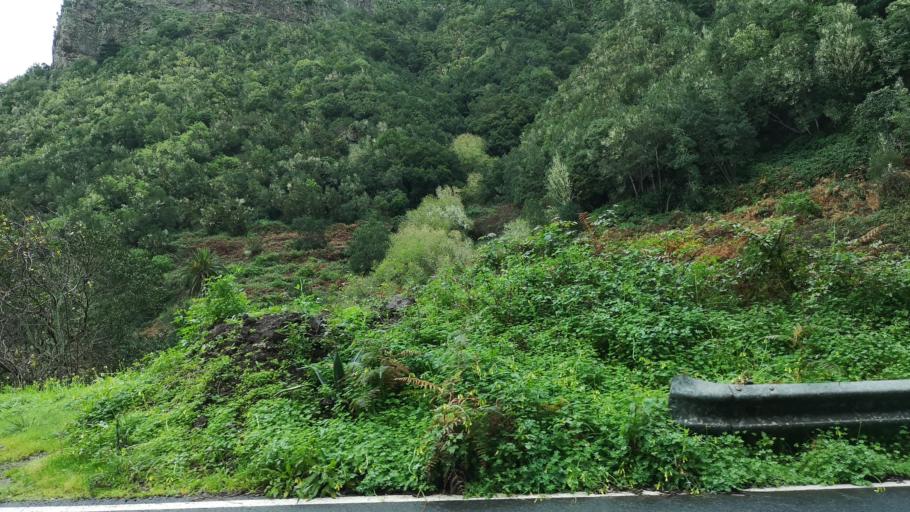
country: ES
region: Canary Islands
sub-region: Provincia de Santa Cruz de Tenerife
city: Hermigua
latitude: 28.1312
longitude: -17.2005
